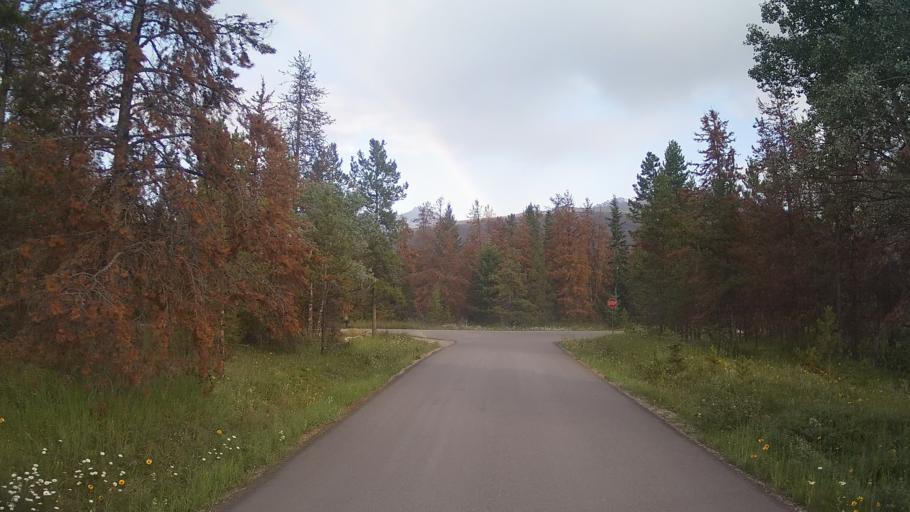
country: CA
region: Alberta
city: Jasper Park Lodge
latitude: 52.9292
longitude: -118.0302
